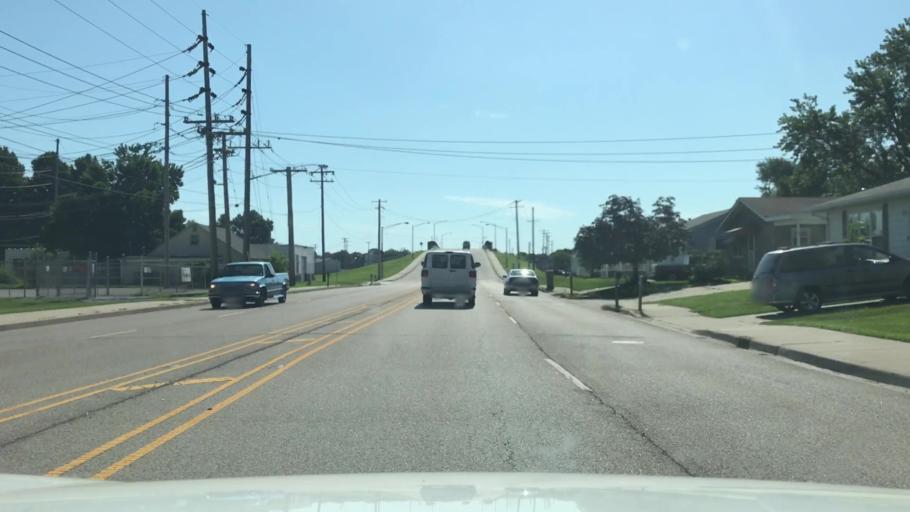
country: US
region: Illinois
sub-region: Madison County
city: Granite City
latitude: 38.7315
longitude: -90.1292
